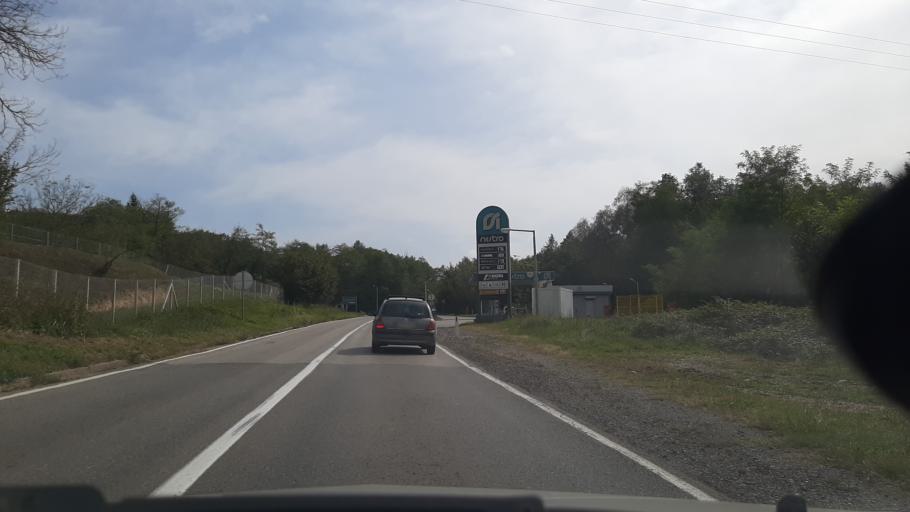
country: BA
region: Republika Srpska
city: Laktasi
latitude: 44.8727
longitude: 17.3312
